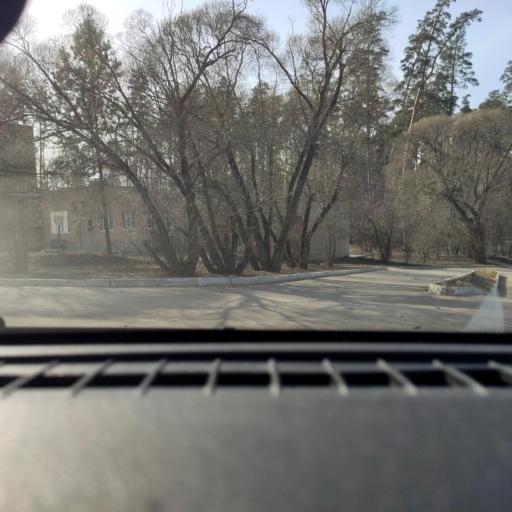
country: RU
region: Samara
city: Tol'yatti
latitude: 53.4986
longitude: 49.3594
